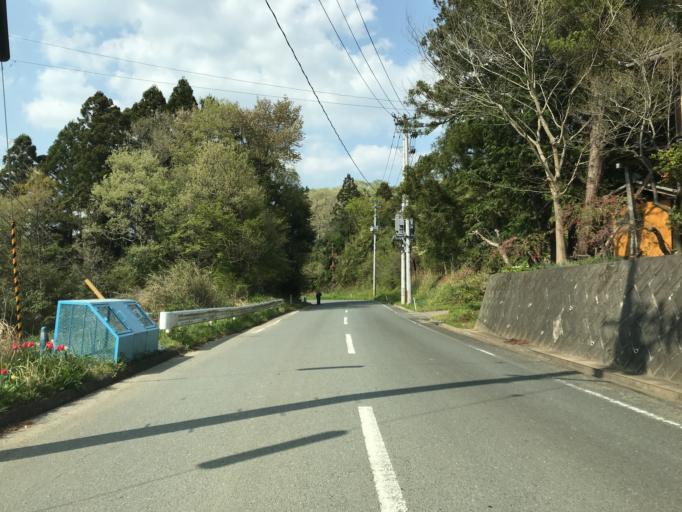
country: JP
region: Fukushima
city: Iwaki
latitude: 36.9815
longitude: 140.7633
